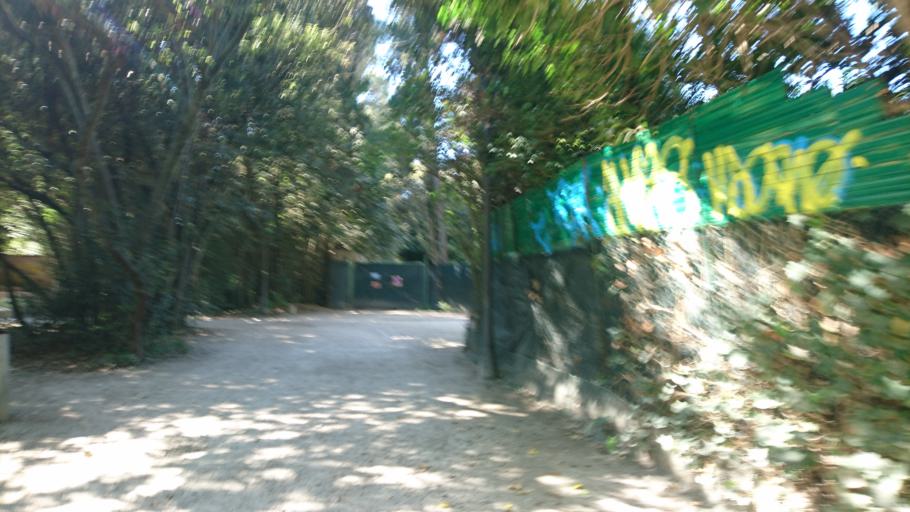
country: IT
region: The Marches
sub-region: Provincia di Pesaro e Urbino
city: Pesaro
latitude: 43.9050
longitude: 12.9012
